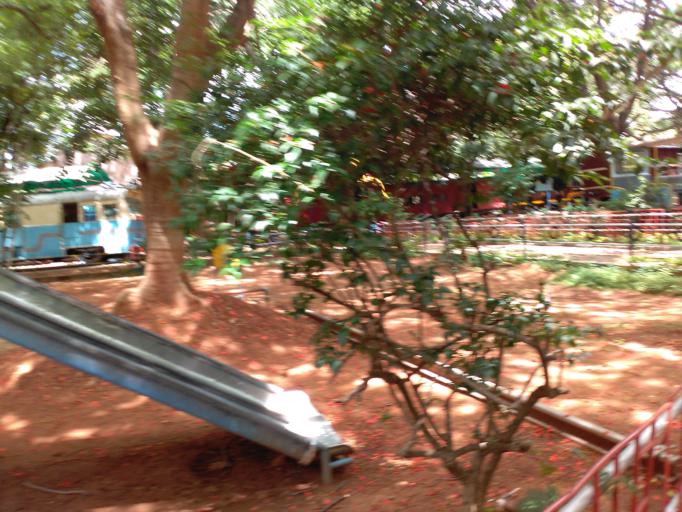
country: IN
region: Karnataka
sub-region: Mysore
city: Mysore
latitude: 12.3151
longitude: 76.6446
